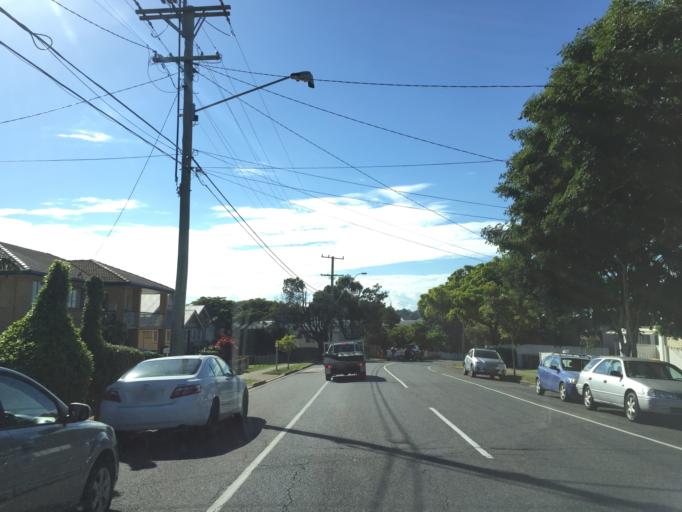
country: AU
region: Queensland
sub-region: Brisbane
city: Wilston
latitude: -27.4377
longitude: 153.0006
